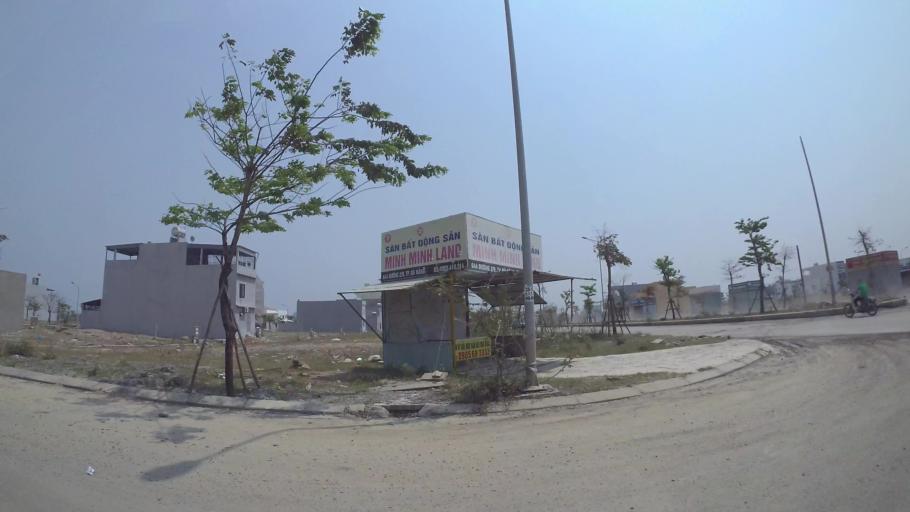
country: VN
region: Da Nang
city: Ngu Hanh Son
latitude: 16.0113
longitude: 108.2405
